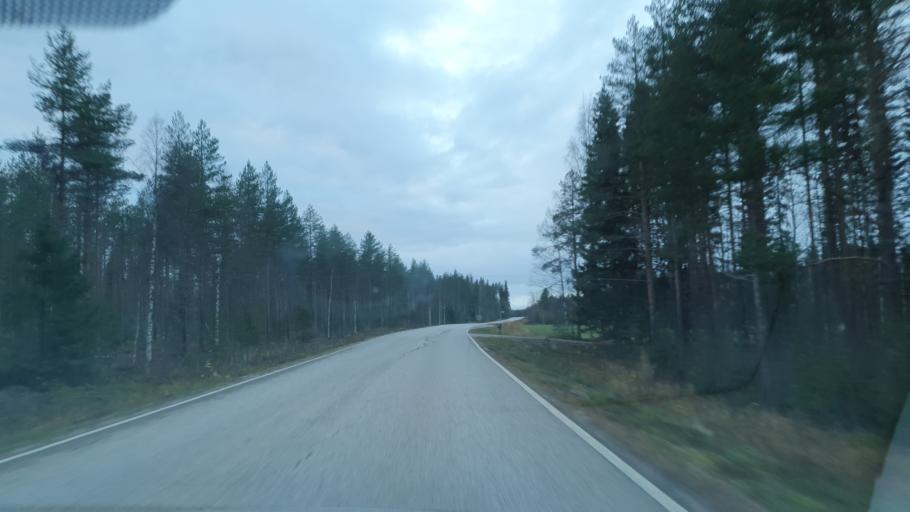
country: FI
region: Kainuu
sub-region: Kajaani
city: Ristijaervi
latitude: 64.4222
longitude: 28.4036
